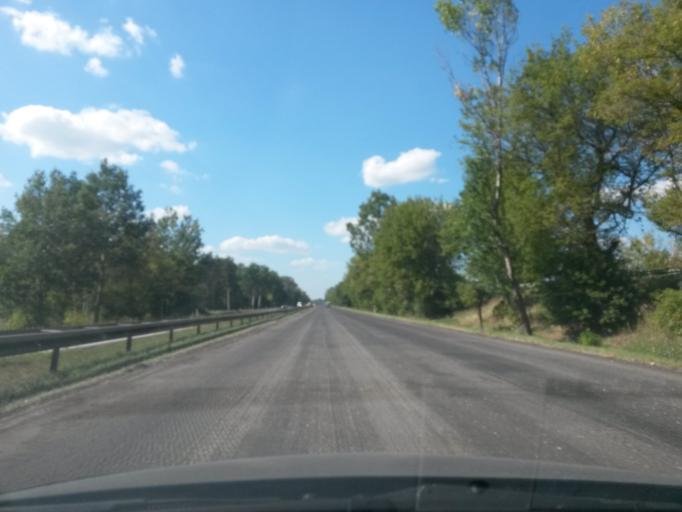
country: PL
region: Masovian Voivodeship
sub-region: Powiat nowodworski
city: Nowy Dwor Mazowiecki
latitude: 52.3986
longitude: 20.7141
